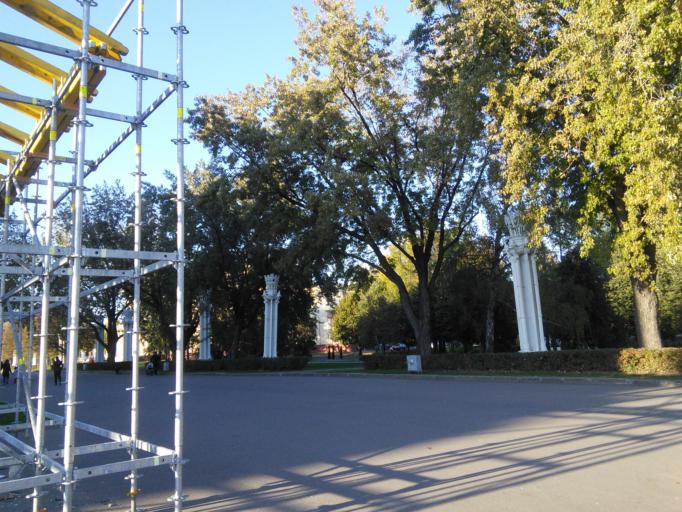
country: RU
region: Moscow
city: Ostankinskiy
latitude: 55.8286
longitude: 37.6348
